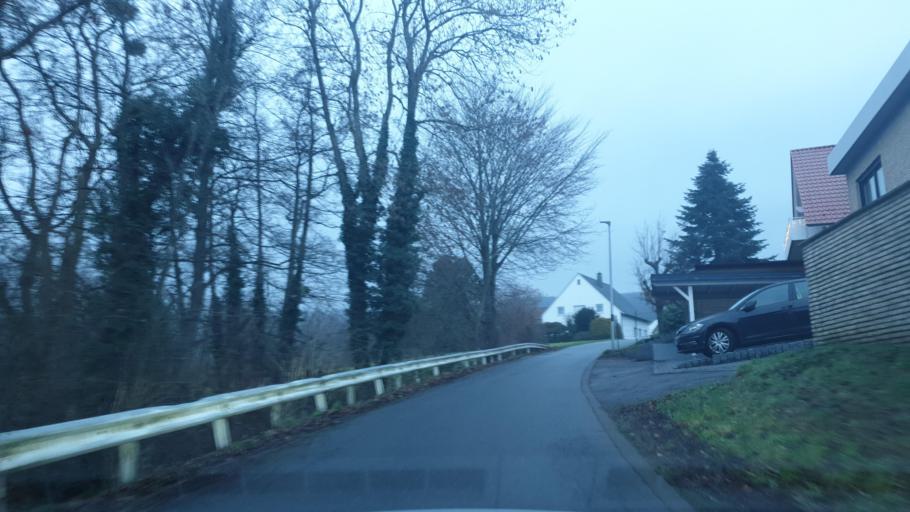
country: DE
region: North Rhine-Westphalia
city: Bad Oeynhausen
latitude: 52.2428
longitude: 8.8398
